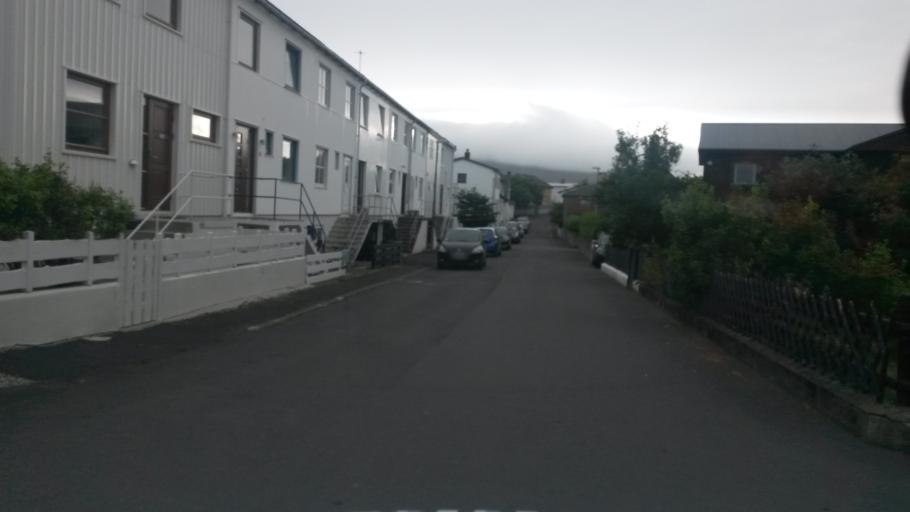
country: FO
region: Streymoy
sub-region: Torshavn
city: Torshavn
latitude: 62.0115
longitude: -6.7608
